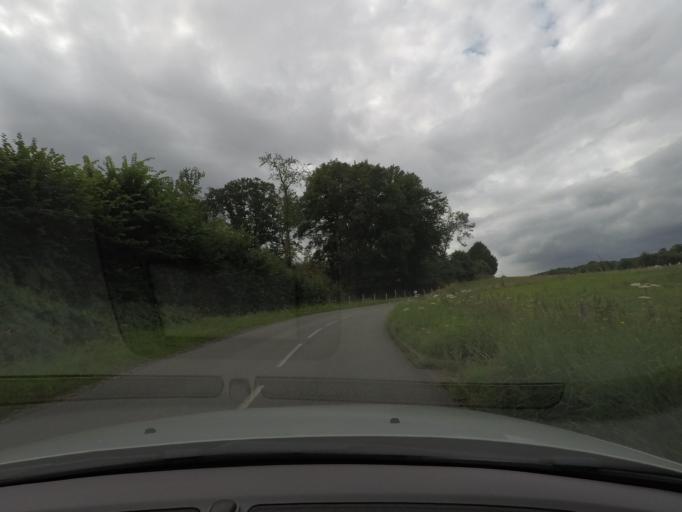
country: FR
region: Haute-Normandie
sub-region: Departement de l'Eure
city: Les Andelys
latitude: 49.2832
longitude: 1.3483
